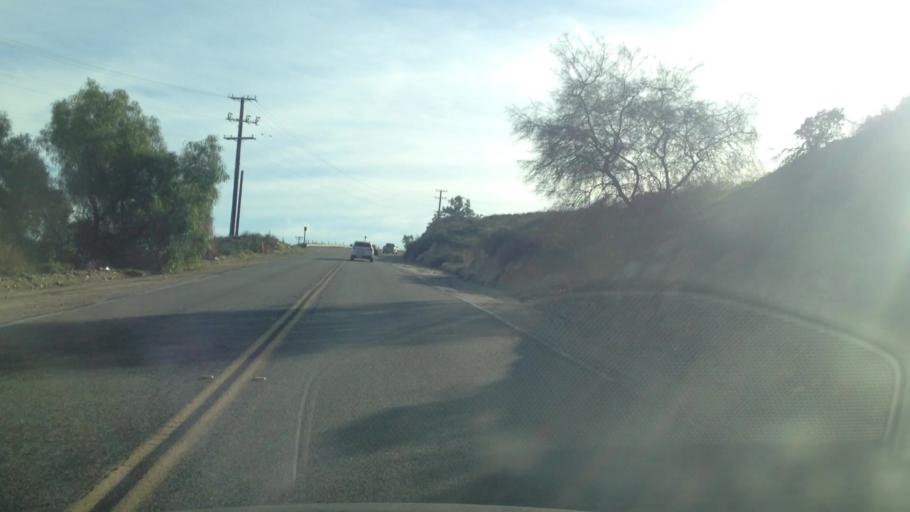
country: US
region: California
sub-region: Riverside County
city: El Cerrito
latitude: 33.8552
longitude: -117.4545
